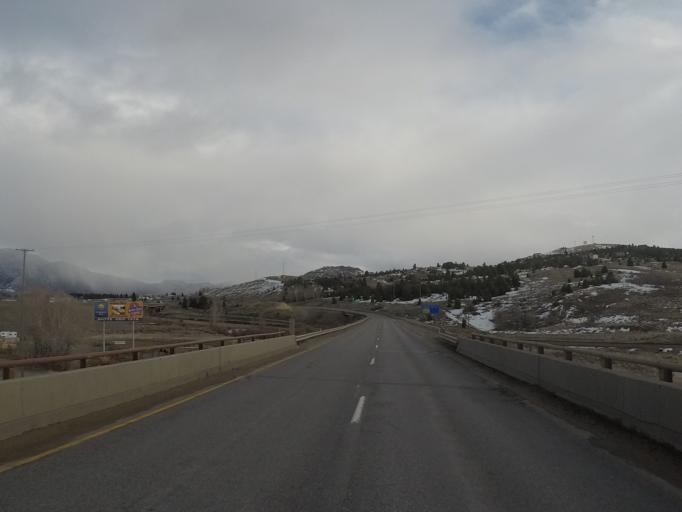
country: US
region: Montana
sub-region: Silver Bow County
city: Butte
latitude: 45.9991
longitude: -112.5684
